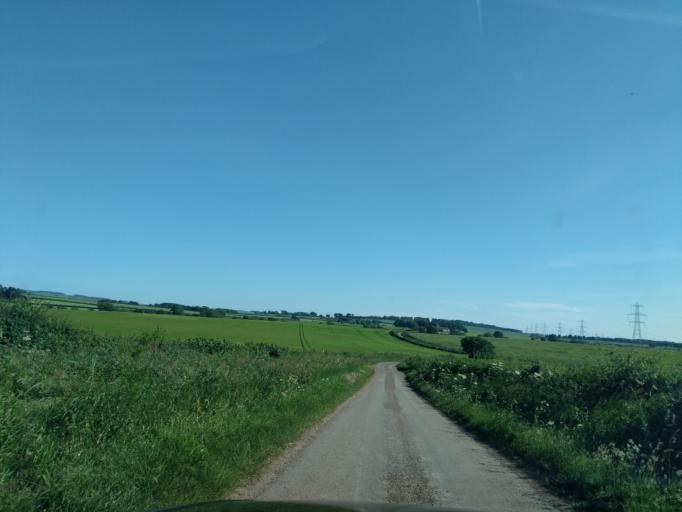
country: GB
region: Scotland
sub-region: East Lothian
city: Ormiston
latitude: 55.8858
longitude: -2.9365
